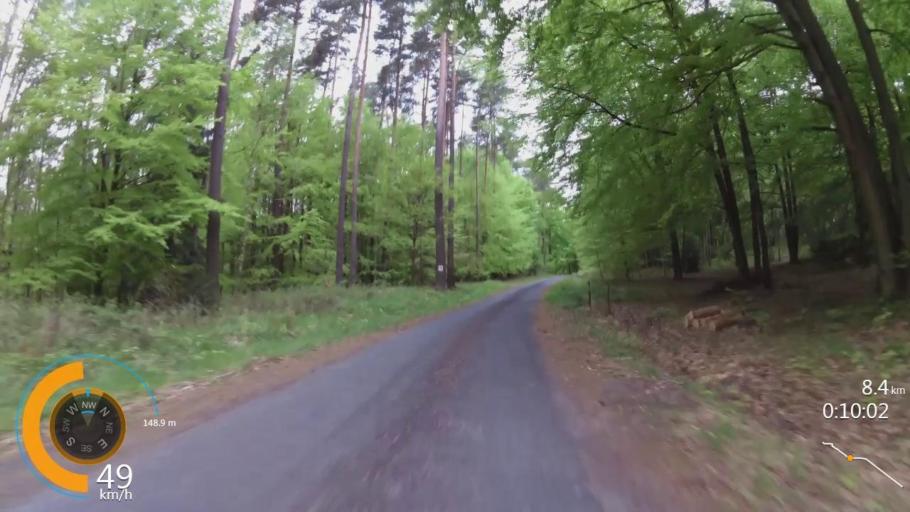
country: PL
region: West Pomeranian Voivodeship
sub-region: Powiat drawski
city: Wierzchowo
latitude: 53.5041
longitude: 16.1279
